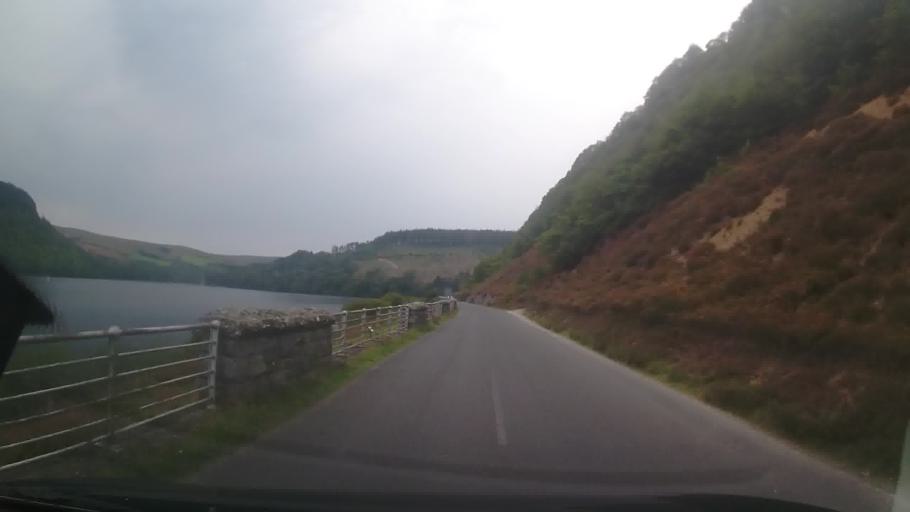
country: GB
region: Wales
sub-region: Sir Powys
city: Rhayader
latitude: 52.2644
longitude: -3.5864
